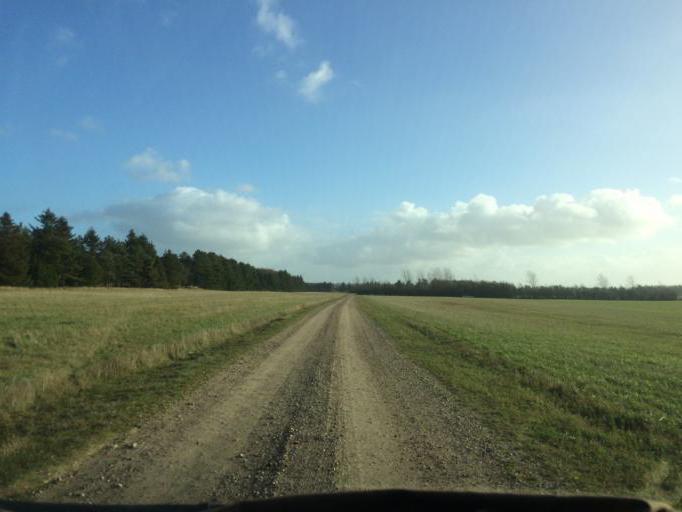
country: DK
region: Central Jutland
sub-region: Holstebro Kommune
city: Ulfborg
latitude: 56.2465
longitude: 8.4360
